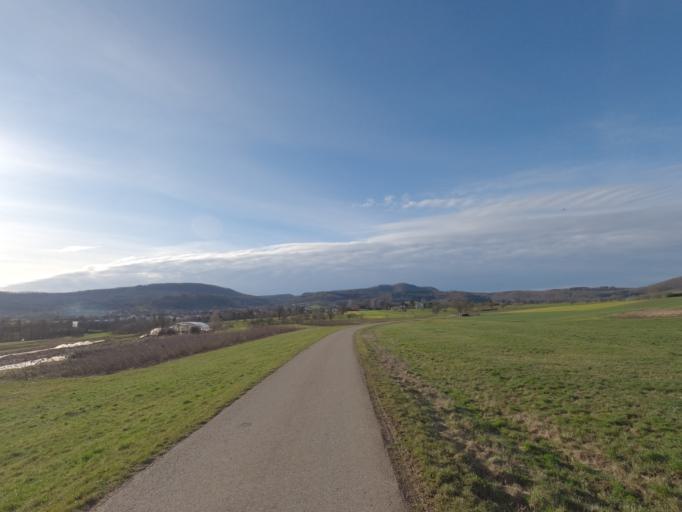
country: DE
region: Baden-Wuerttemberg
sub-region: Regierungsbezirk Stuttgart
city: Boll
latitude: 48.6532
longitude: 9.6087
